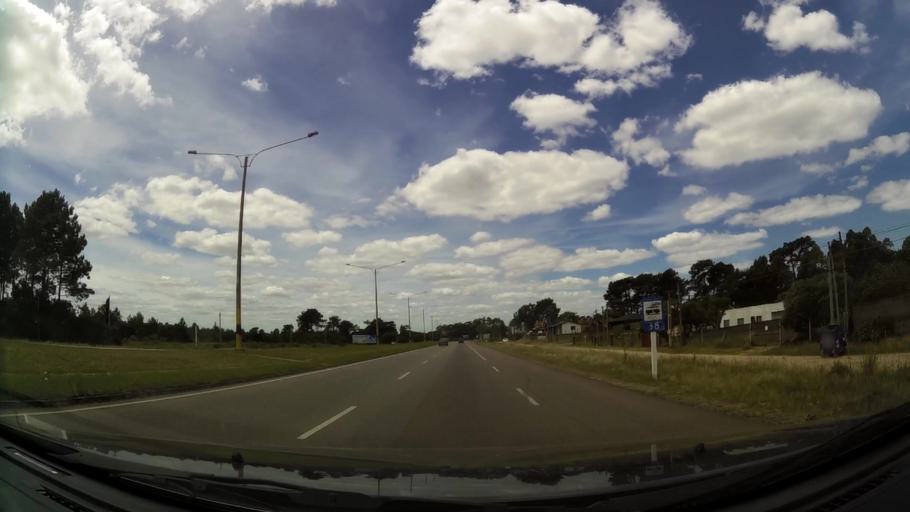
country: UY
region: Canelones
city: Pando
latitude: -34.7950
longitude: -55.9055
